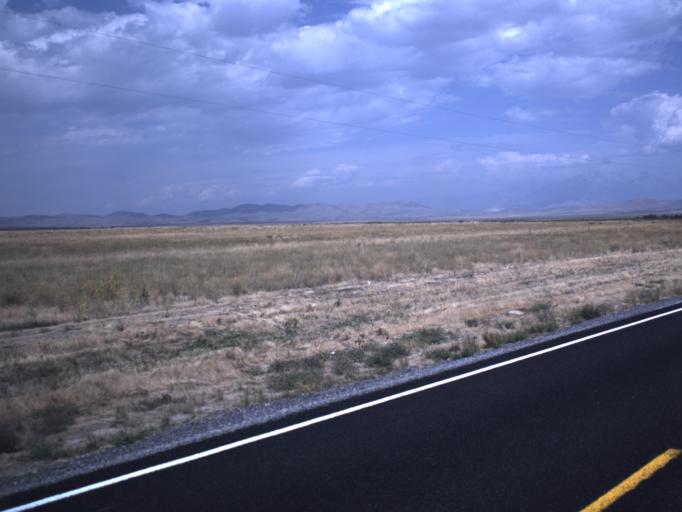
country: US
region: Utah
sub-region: Utah County
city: Eagle Mountain
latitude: 40.2512
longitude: -112.1187
